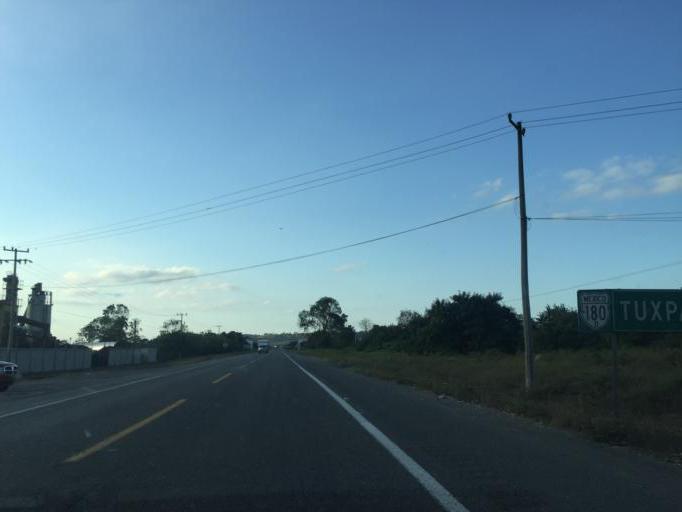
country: MX
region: Veracruz
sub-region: Papantla
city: Residencial Tajin
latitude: 20.6280
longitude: -97.3931
